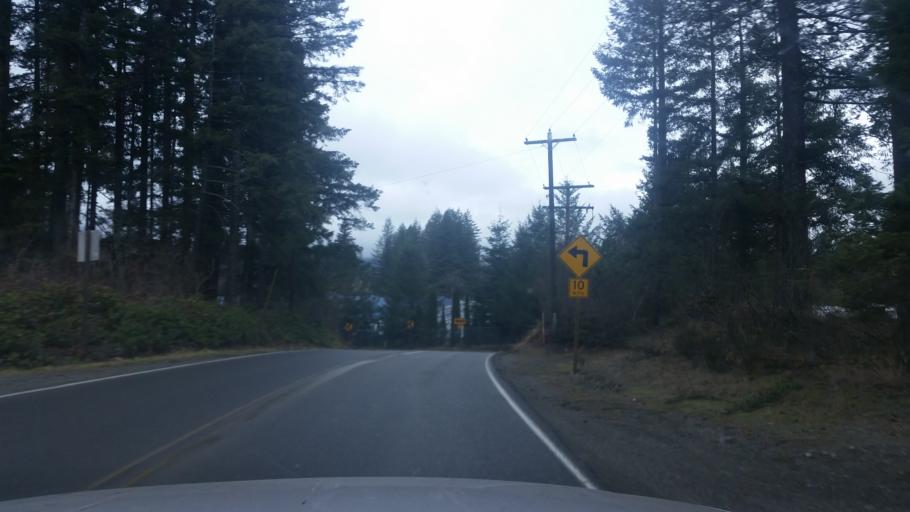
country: US
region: Washington
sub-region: King County
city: Tanner
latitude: 47.4746
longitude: -121.7398
